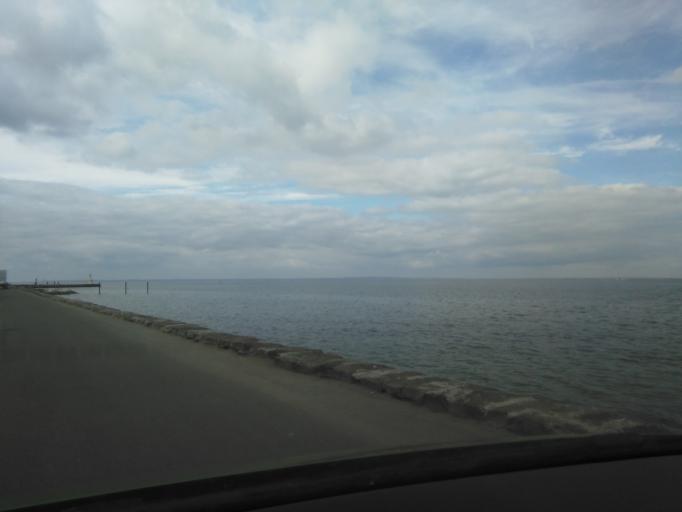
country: DK
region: South Denmark
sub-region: Nordfyns Kommune
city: Bogense
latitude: 55.5686
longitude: 10.0805
